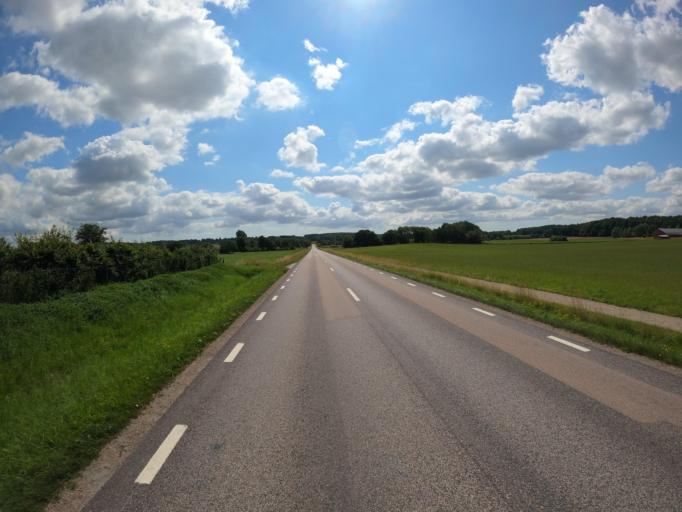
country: SE
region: Skane
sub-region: Lunds Kommun
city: Veberod
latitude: 55.6005
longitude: 13.4901
